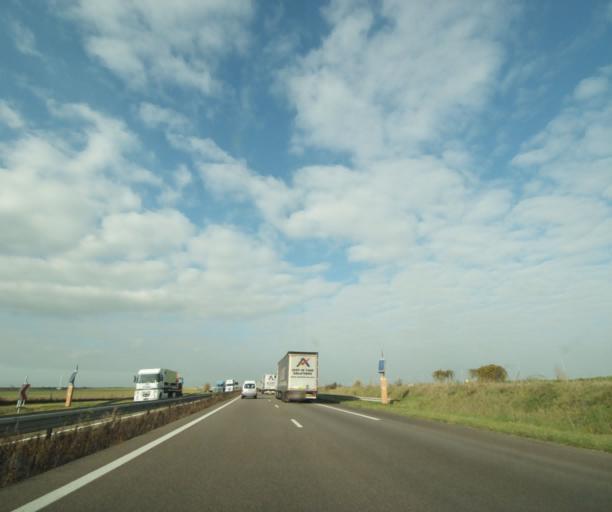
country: FR
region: Champagne-Ardenne
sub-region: Departement de la Marne
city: Verzy
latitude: 49.1652
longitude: 4.1869
